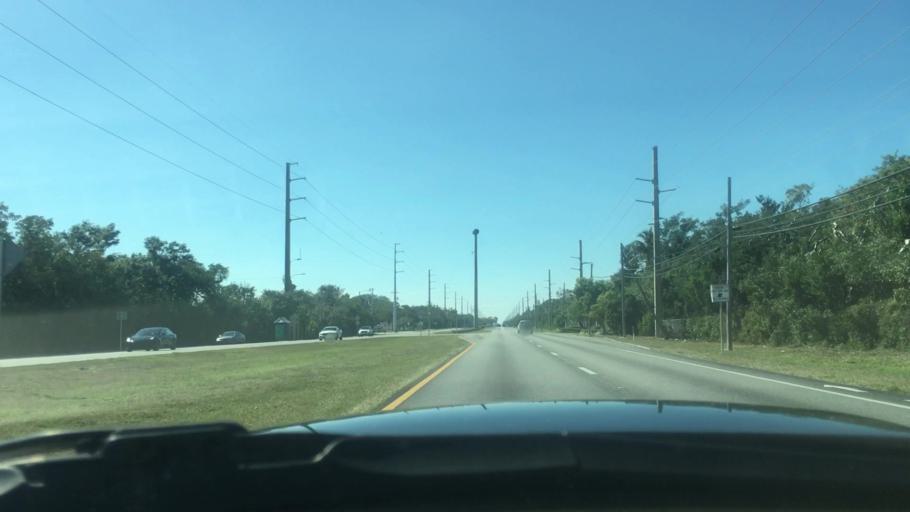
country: US
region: Florida
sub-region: Monroe County
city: Key Largo
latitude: 25.0621
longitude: -80.4748
